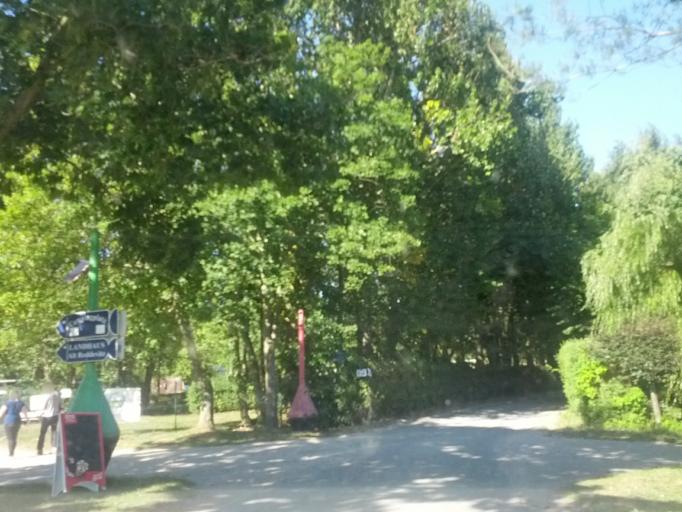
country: DE
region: Mecklenburg-Vorpommern
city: Ostseebad Sellin
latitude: 54.3354
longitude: 13.6824
